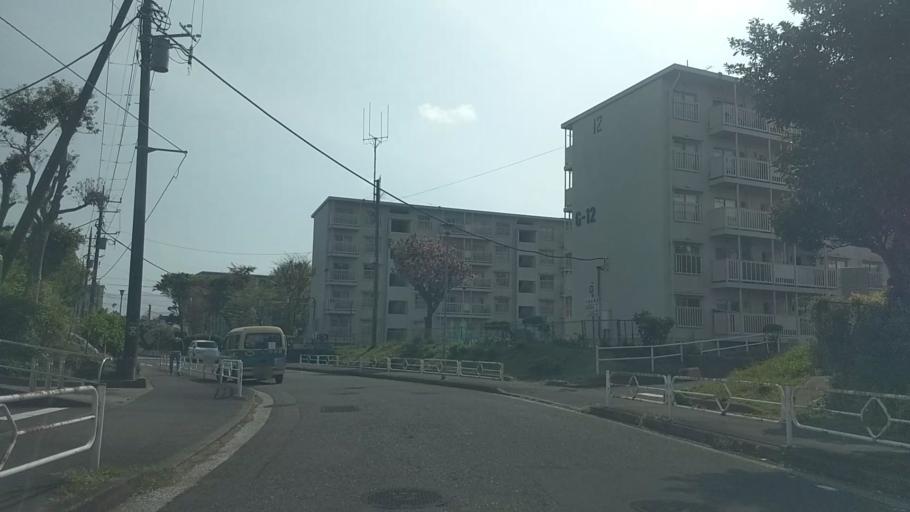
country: JP
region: Kanagawa
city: Kamakura
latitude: 35.3849
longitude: 139.5706
